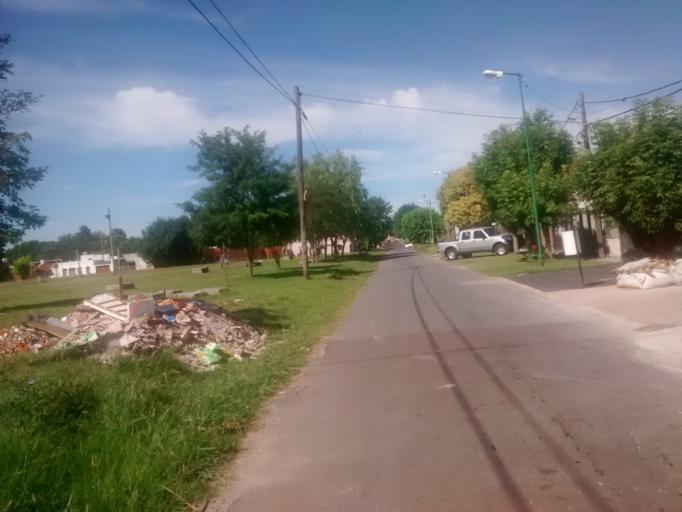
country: AR
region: Buenos Aires
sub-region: Partido de La Plata
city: La Plata
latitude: -34.9472
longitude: -57.9367
